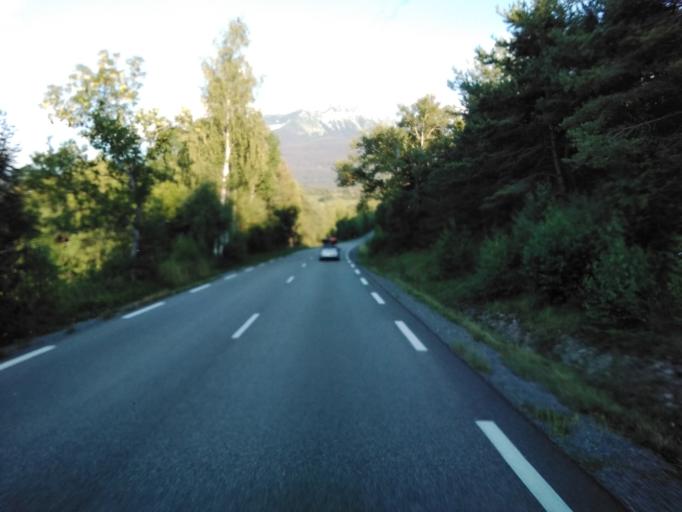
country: FR
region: Provence-Alpes-Cote d'Azur
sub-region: Departement des Alpes-de-Haute-Provence
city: Seyne-les-Alpes
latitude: 44.4502
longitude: 6.3226
